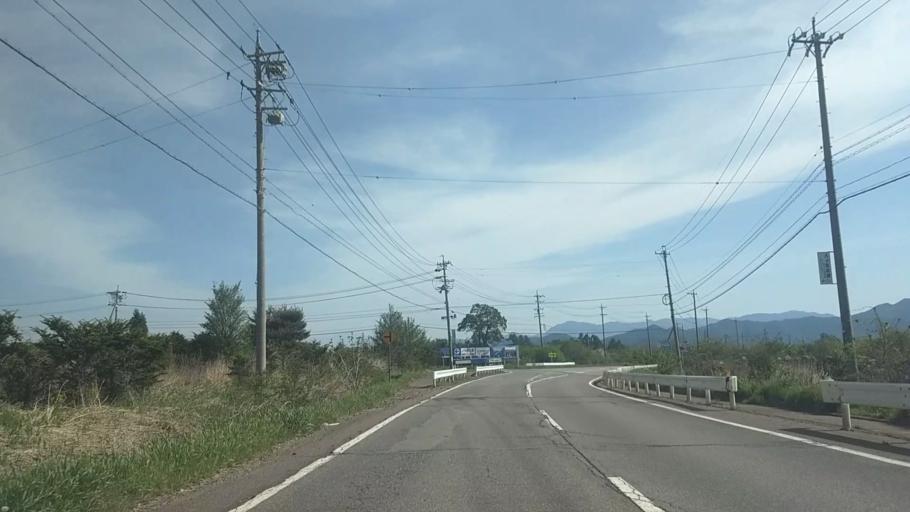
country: JP
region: Nagano
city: Saku
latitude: 35.9857
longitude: 138.4855
